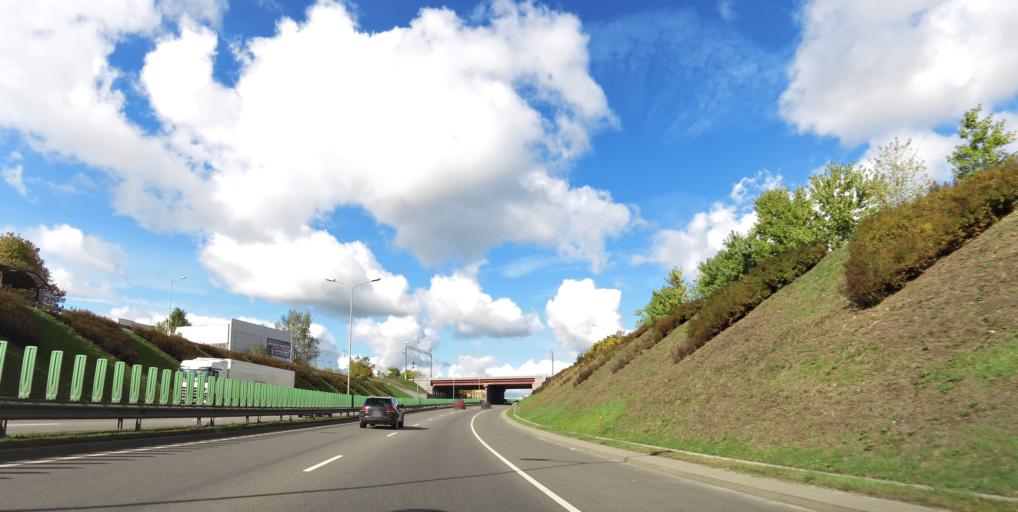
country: LT
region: Vilnius County
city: Vilkpede
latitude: 54.6624
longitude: 25.2570
